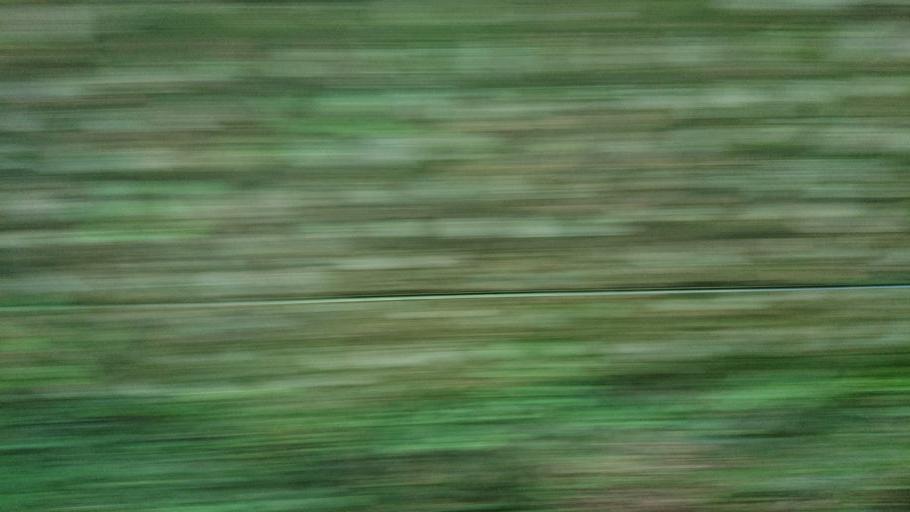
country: TW
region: Taiwan
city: Daxi
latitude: 24.8861
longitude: 121.3773
